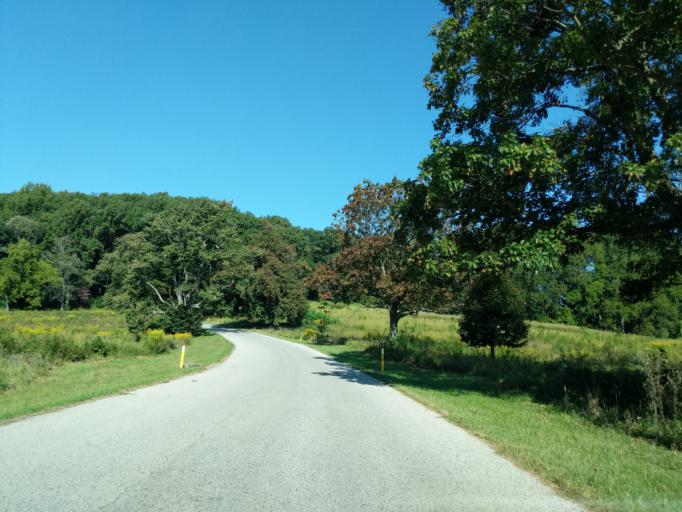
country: US
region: Pennsylvania
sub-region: Chester County
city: Chesterbrook
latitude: 40.0896
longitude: -75.4466
